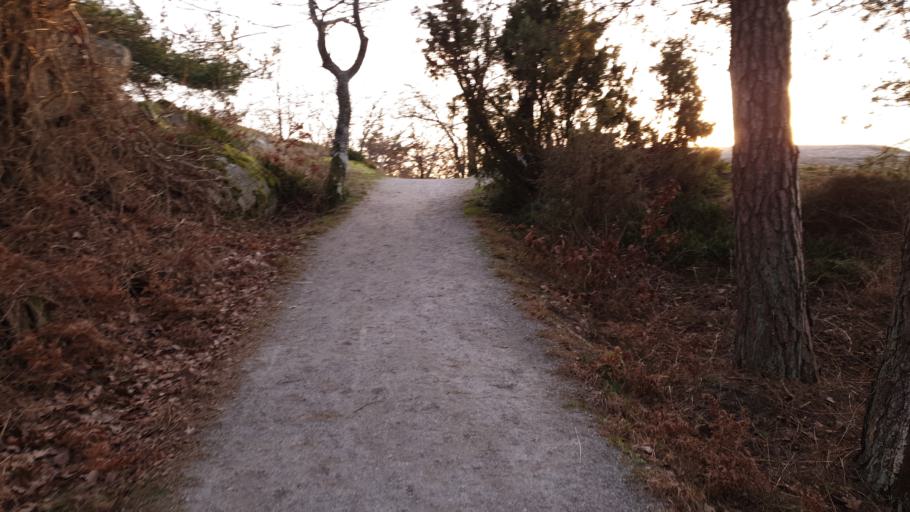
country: SE
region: Blekinge
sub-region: Karlshamns Kommun
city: Karlshamn
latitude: 56.1588
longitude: 14.8783
